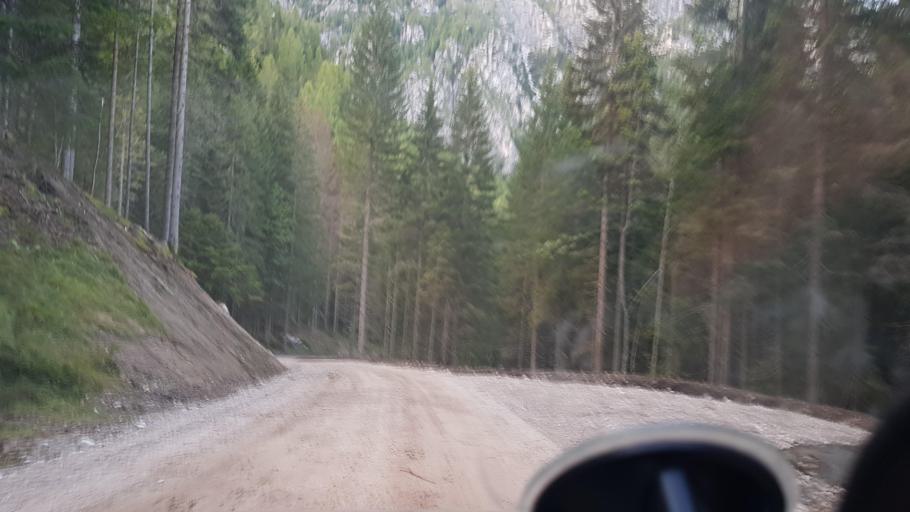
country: IT
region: Veneto
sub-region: Provincia di Belluno
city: San Pietro di Cadore
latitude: 46.6061
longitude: 12.5942
